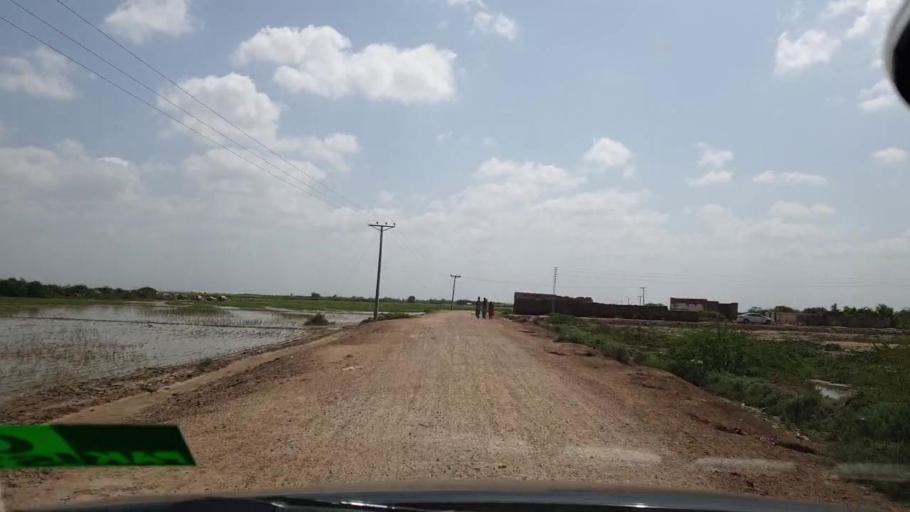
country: PK
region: Sindh
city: Kadhan
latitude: 24.6155
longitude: 69.1856
